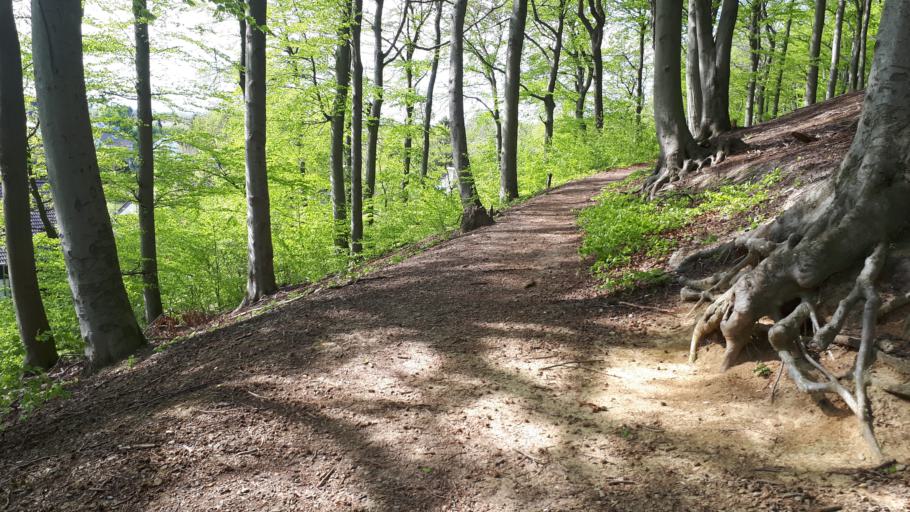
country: DE
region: North Rhine-Westphalia
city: Castrop-Rauxel
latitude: 51.5419
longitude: 7.3246
